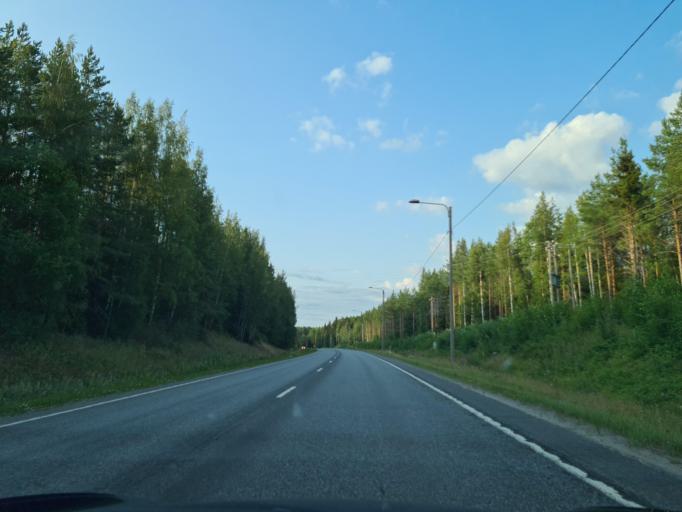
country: FI
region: Southern Ostrobothnia
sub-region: Seinaejoki
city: Kauhava
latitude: 63.0735
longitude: 23.0542
